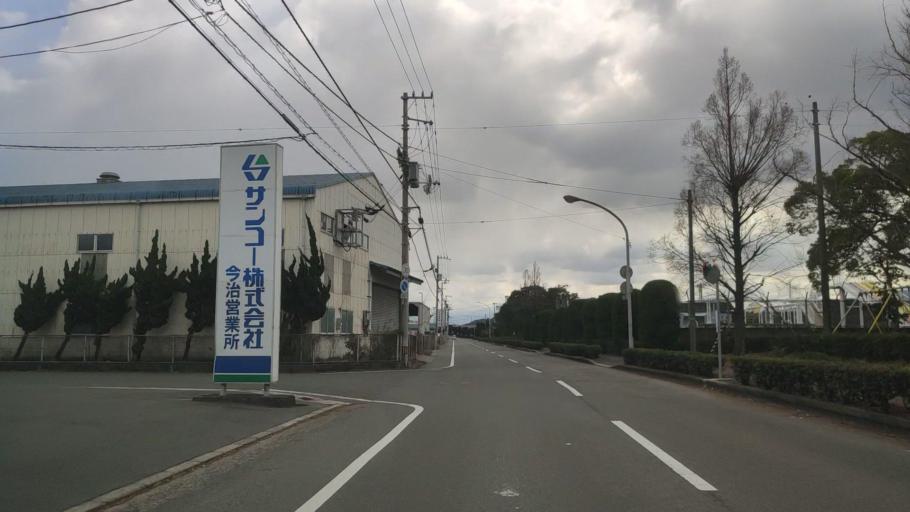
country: JP
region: Ehime
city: Saijo
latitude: 34.0551
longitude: 133.0217
